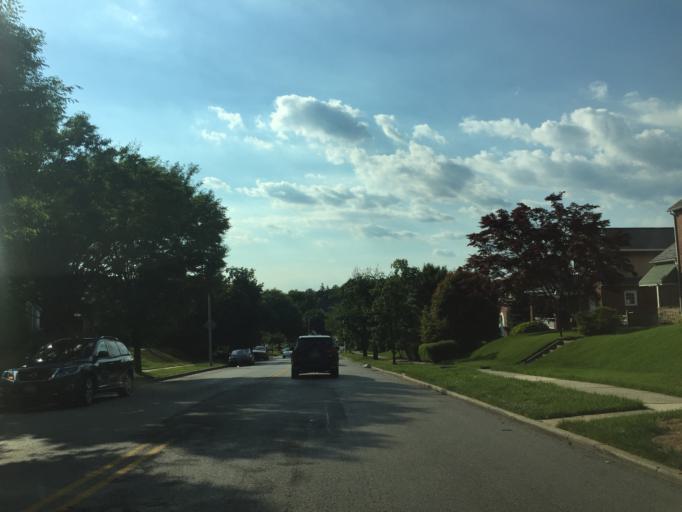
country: US
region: Maryland
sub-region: Baltimore County
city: Parkville
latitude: 39.3382
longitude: -76.5660
